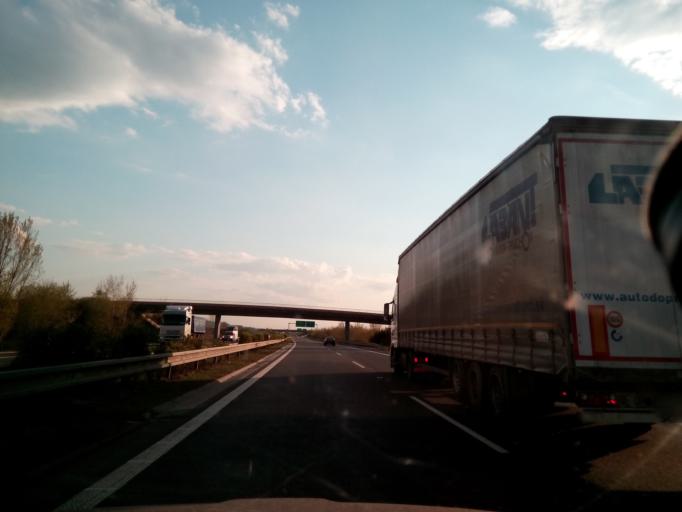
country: SK
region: Nitriansky
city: Ilava
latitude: 49.0057
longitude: 18.2293
